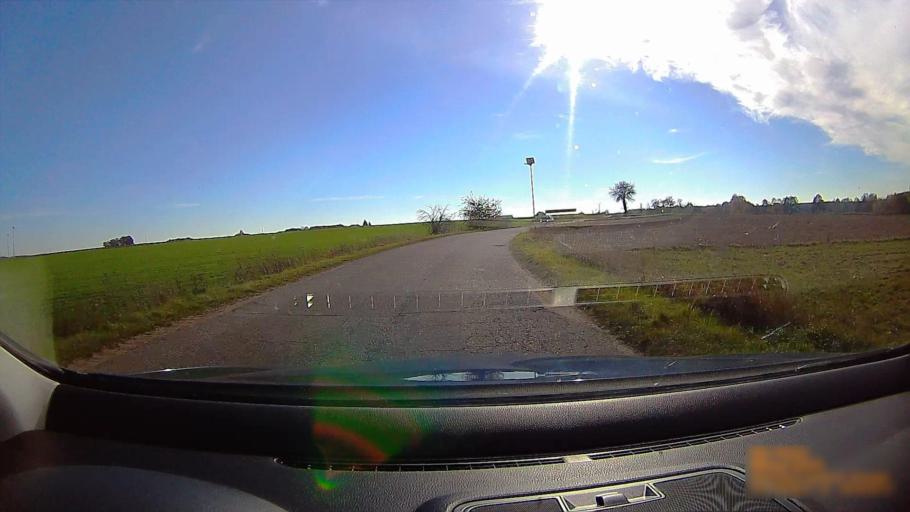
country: PL
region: Greater Poland Voivodeship
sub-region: Powiat ostrzeszowski
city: Doruchow
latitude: 51.3993
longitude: 18.0300
